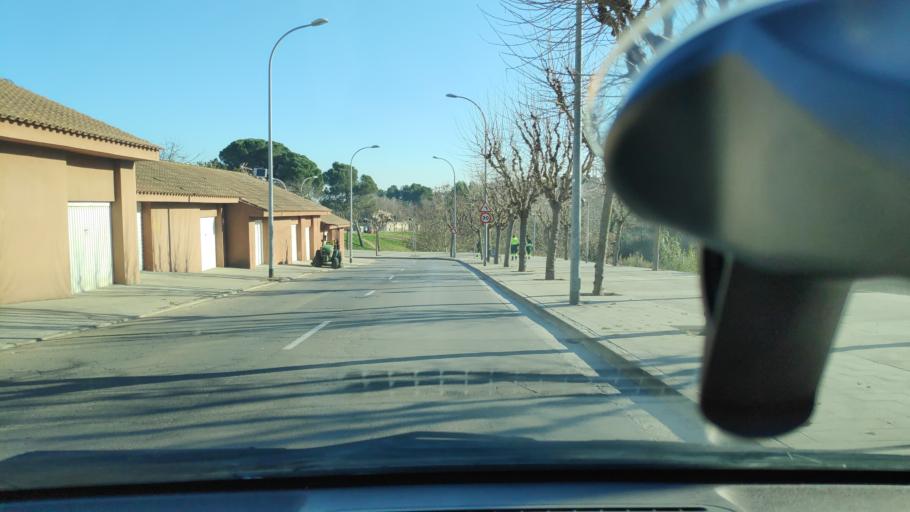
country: ES
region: Catalonia
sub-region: Provincia de Barcelona
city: Sant Quirze del Valles
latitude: 41.5332
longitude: 2.0717
